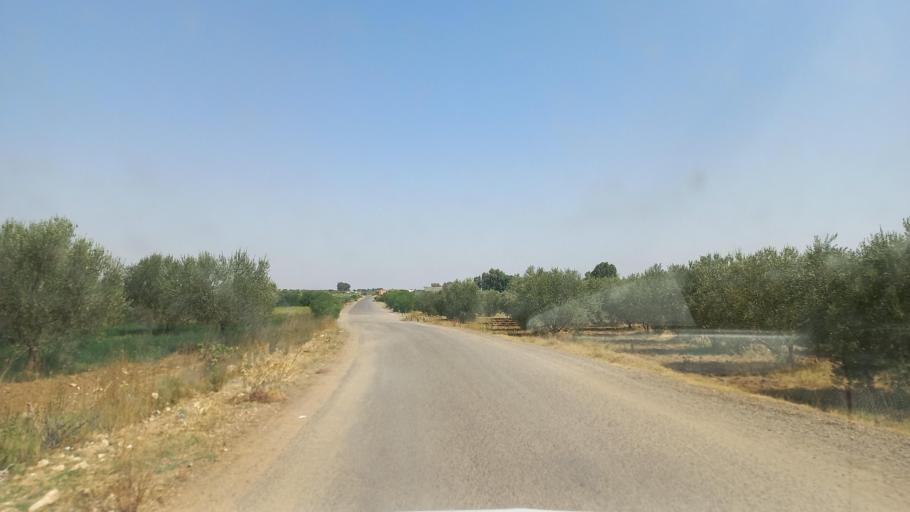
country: TN
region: Al Qasrayn
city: Kasserine
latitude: 35.2360
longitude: 9.0364
